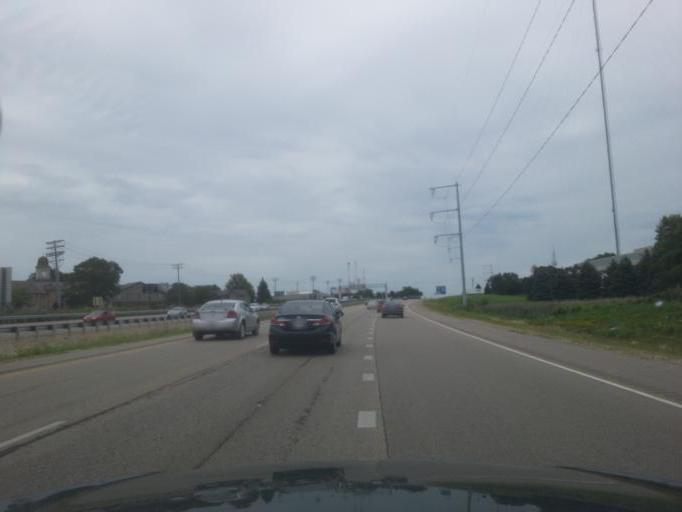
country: US
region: Wisconsin
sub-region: Dane County
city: Middleton
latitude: 43.0531
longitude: -89.4931
